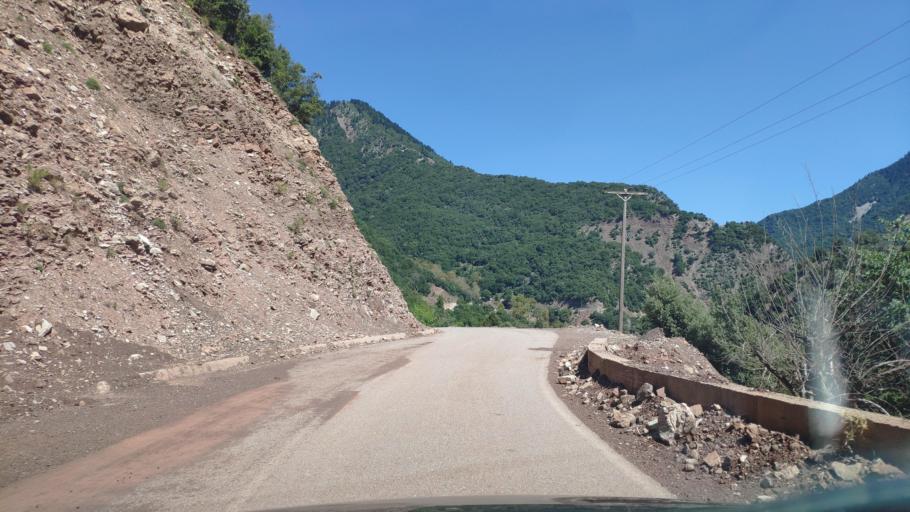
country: GR
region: Central Greece
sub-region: Nomos Evrytanias
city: Kerasochori
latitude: 39.0829
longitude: 21.5966
